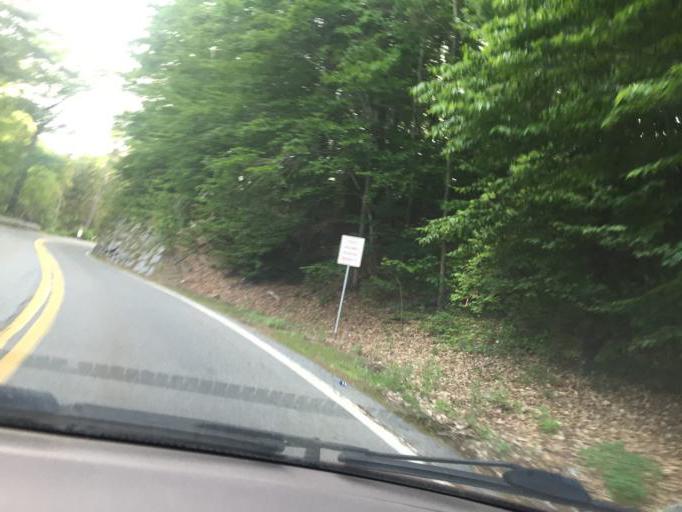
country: US
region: Massachusetts
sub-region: Middlesex County
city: Ashby
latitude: 42.6635
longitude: -71.7911
